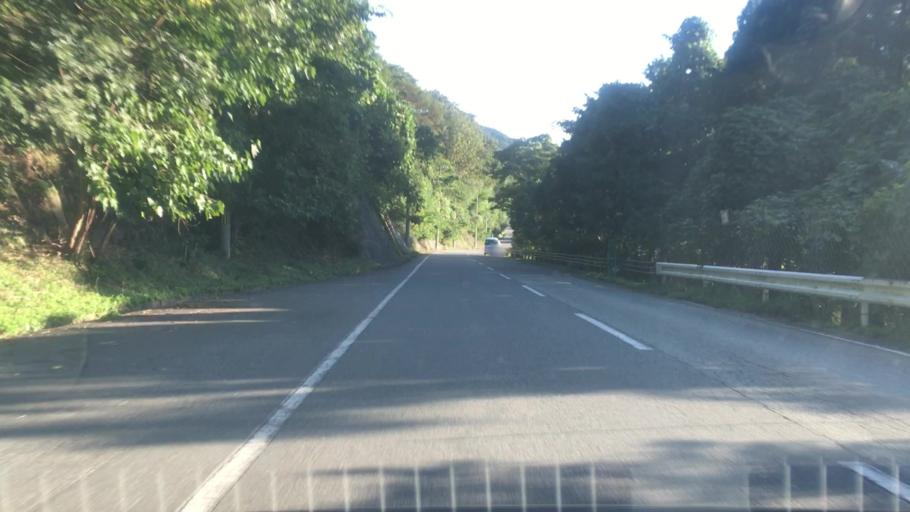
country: JP
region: Hyogo
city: Toyooka
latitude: 35.6054
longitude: 134.8059
